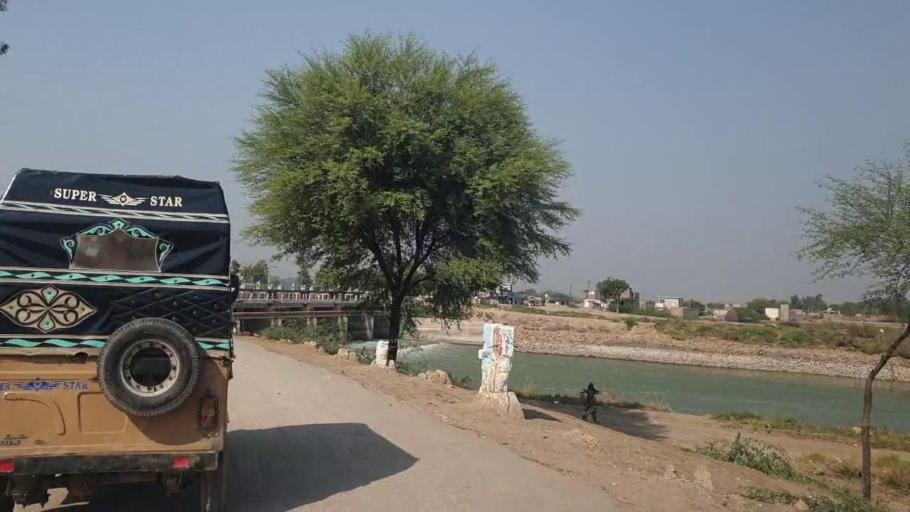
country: PK
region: Sindh
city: Jamshoro
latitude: 25.4396
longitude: 68.3335
